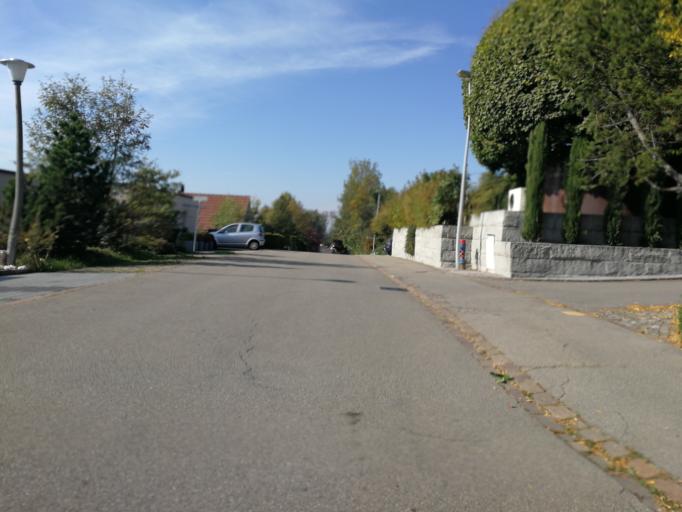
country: CH
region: Zurich
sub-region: Bezirk Hinwil
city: Hadlikon
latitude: 47.2768
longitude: 8.8740
